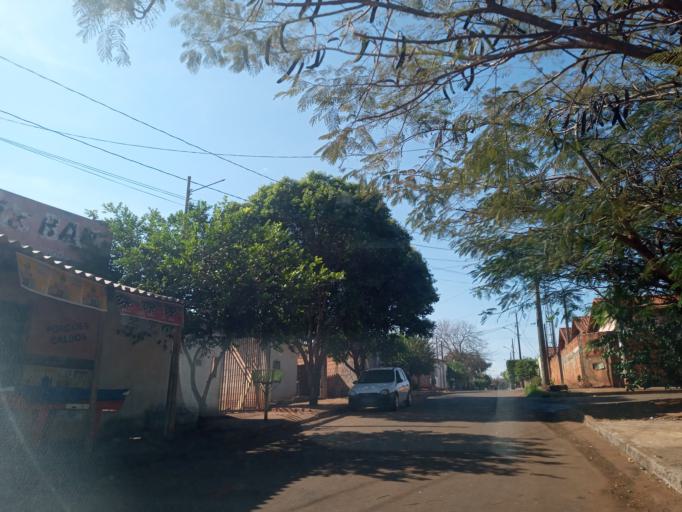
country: BR
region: Minas Gerais
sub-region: Ituiutaba
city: Ituiutaba
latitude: -18.9524
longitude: -49.4637
